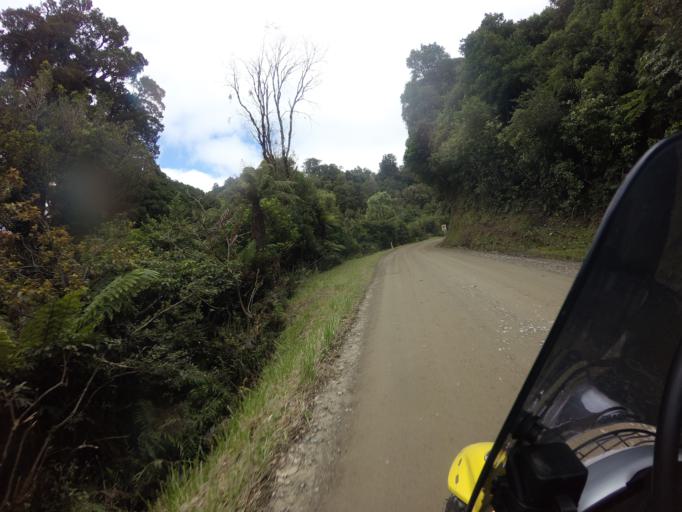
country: NZ
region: Hawke's Bay
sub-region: Wairoa District
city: Wairoa
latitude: -38.7172
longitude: 177.0640
